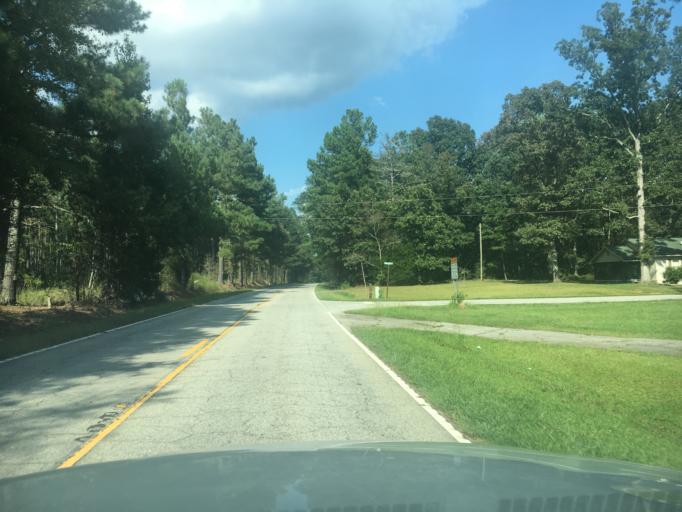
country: US
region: South Carolina
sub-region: Anderson County
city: Pendleton
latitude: 34.6751
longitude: -82.7573
